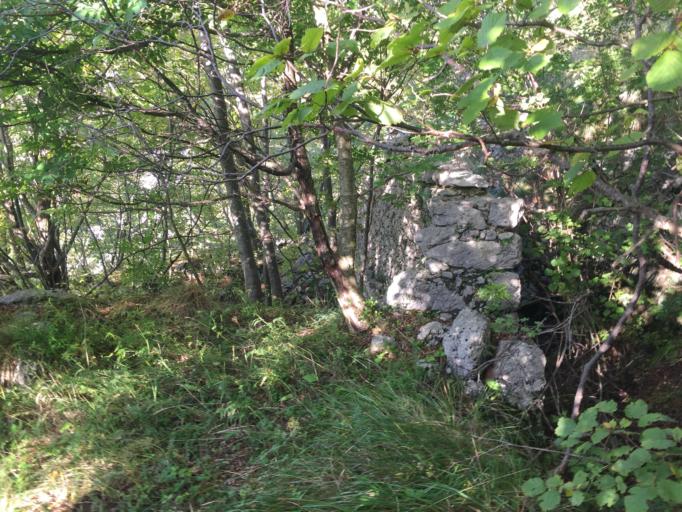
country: IT
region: Friuli Venezia Giulia
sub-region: Provincia di Udine
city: Venzone
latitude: 46.3443
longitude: 13.1846
